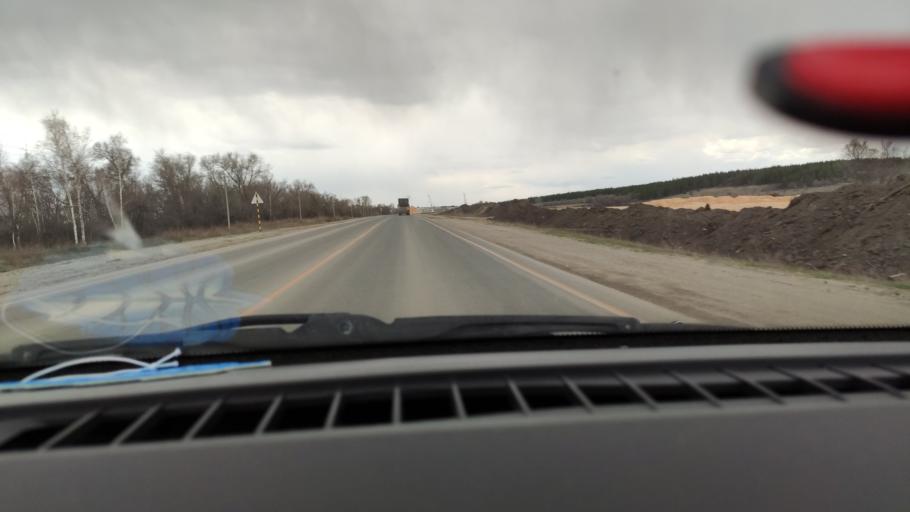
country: RU
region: Saratov
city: Sinodskoye
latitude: 52.0156
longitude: 46.6976
